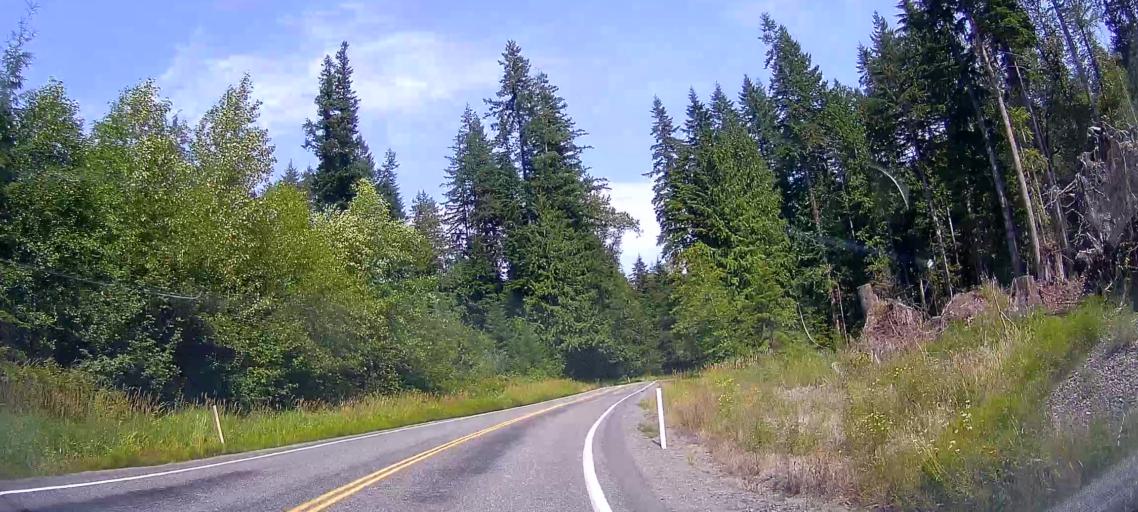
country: US
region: Washington
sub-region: Snohomish County
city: Bryant
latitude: 48.3443
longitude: -122.1075
